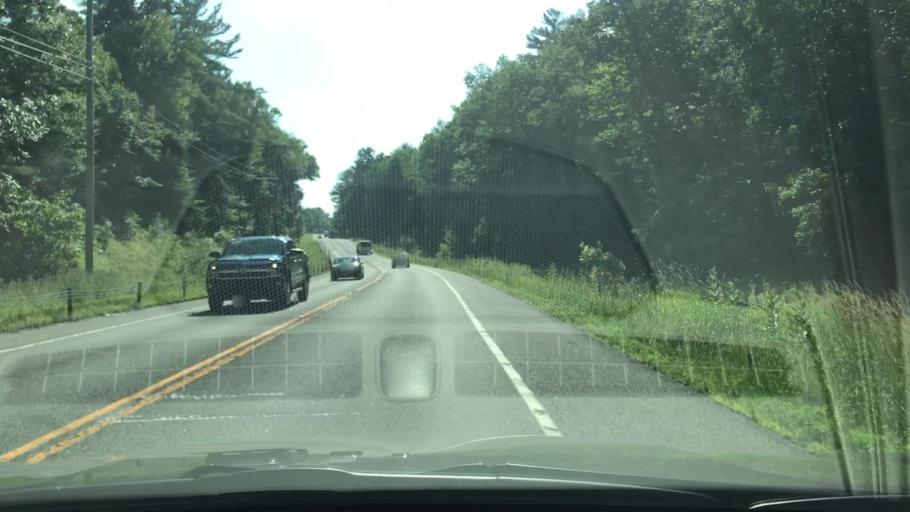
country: US
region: New York
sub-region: Warren County
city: Glens Falls North
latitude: 43.3728
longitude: -73.6837
